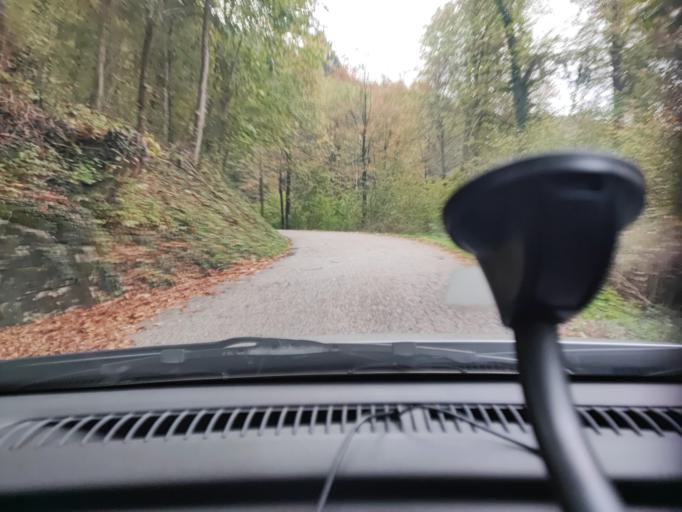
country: SI
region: Kanal
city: Kanal
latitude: 46.0734
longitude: 13.6493
